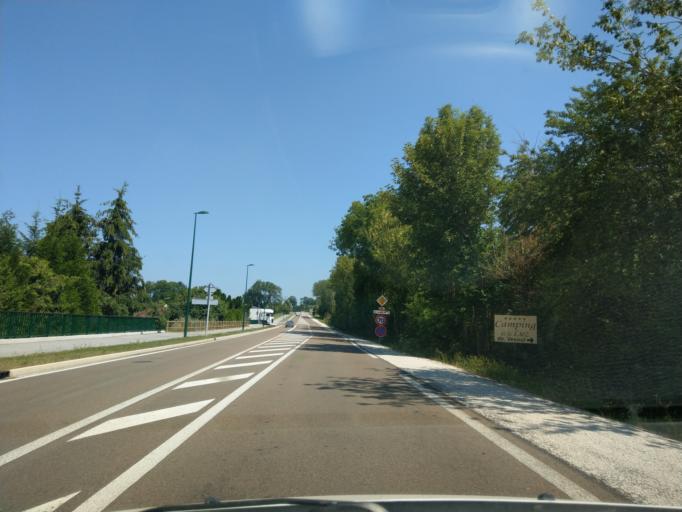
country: FR
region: Champagne-Ardenne
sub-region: Departement de la Haute-Marne
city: Langres
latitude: 47.8396
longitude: 5.3321
